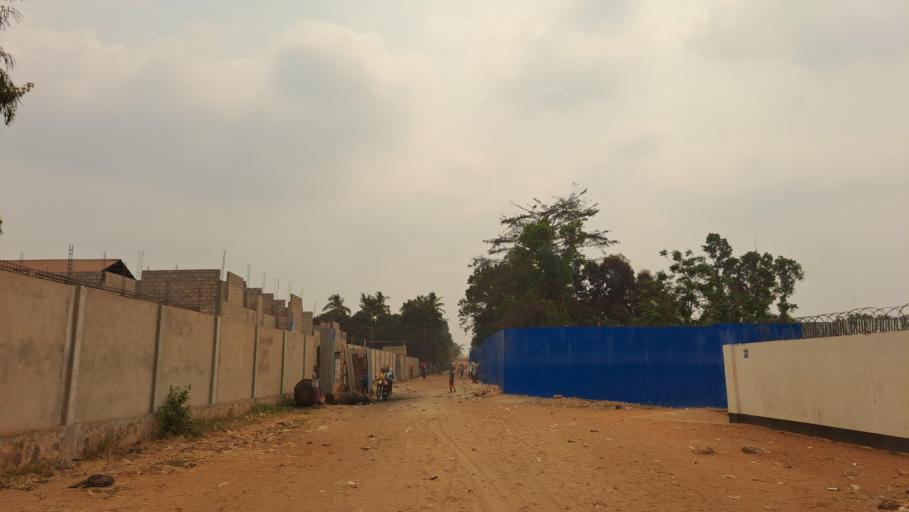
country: CD
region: Kasai-Oriental
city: Mbuji-Mayi
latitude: -6.1150
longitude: 23.5998
